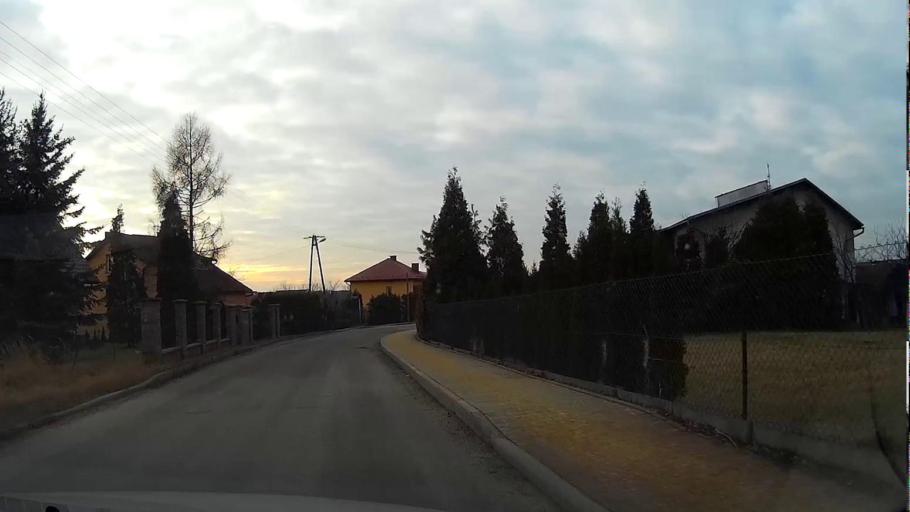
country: PL
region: Lesser Poland Voivodeship
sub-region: Powiat chrzanowski
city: Alwernia
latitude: 50.0640
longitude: 19.5351
